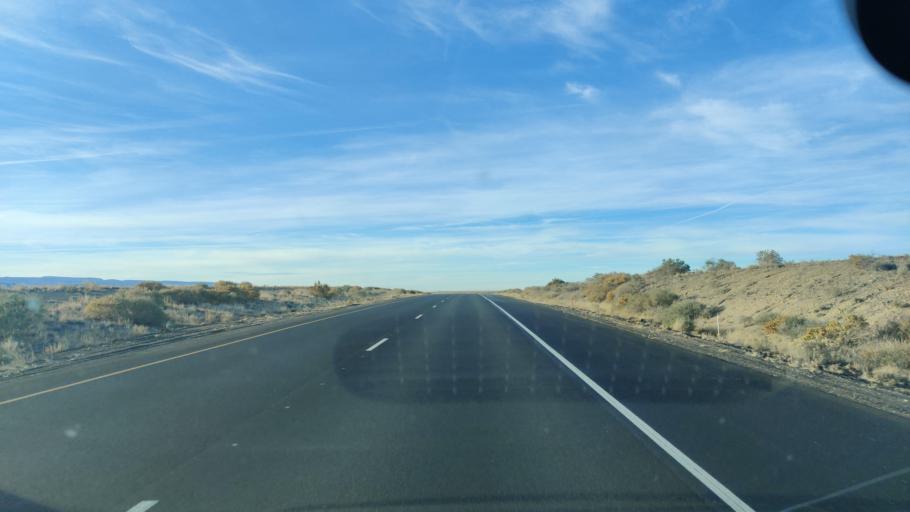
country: US
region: Colorado
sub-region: Delta County
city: Delta
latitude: 38.7999
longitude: -108.2675
